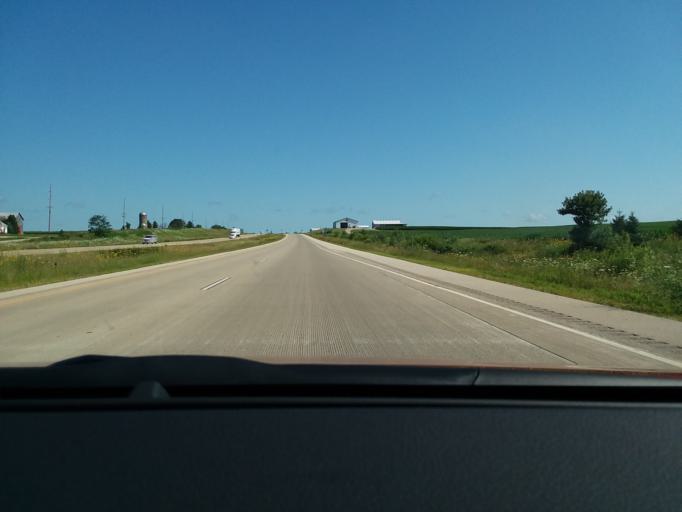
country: US
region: Wisconsin
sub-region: Dane County
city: Windsor
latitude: 43.2234
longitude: -89.3226
